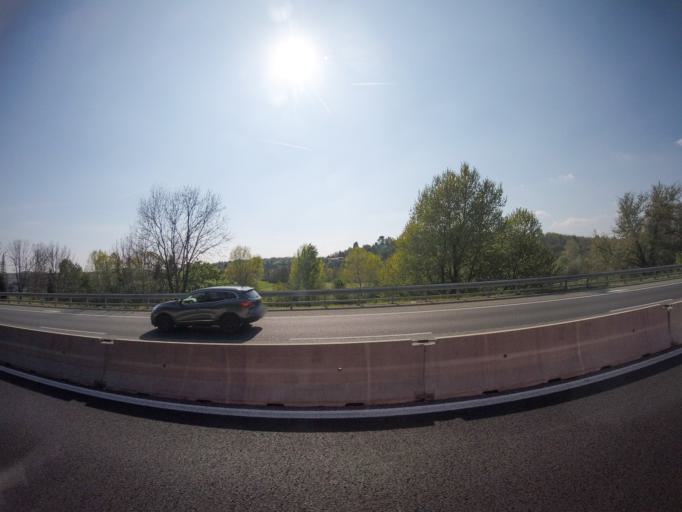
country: IT
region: Lombardy
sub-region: Provincia di Como
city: Lucino
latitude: 45.7892
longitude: 9.0490
